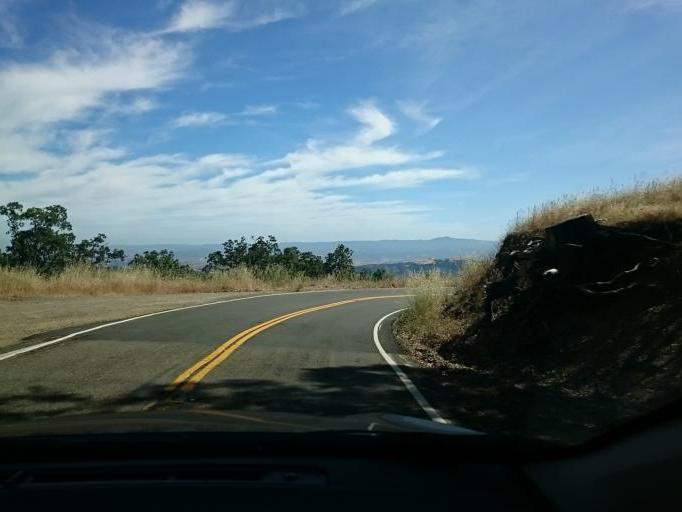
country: US
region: California
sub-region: Santa Clara County
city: East Foothills
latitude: 37.3395
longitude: -121.6519
